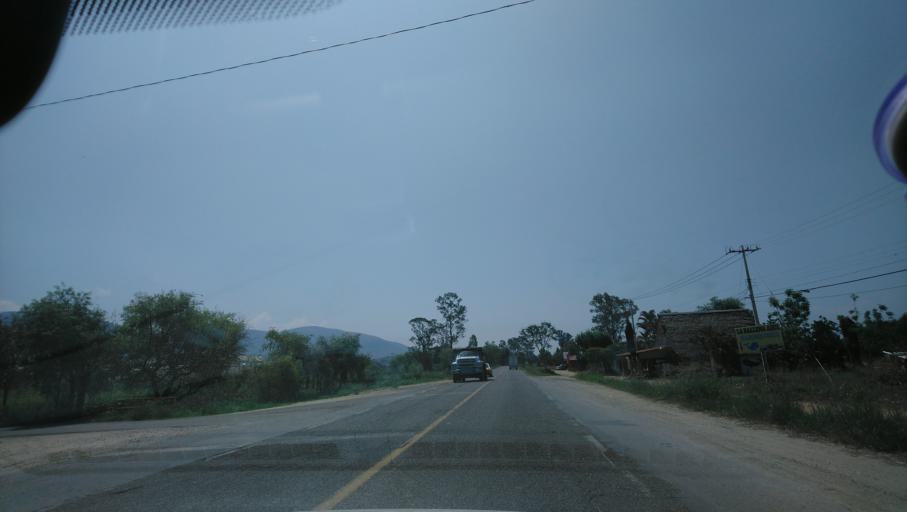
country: MX
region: Oaxaca
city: Santa Maria del Tule
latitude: 17.0435
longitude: -96.6300
